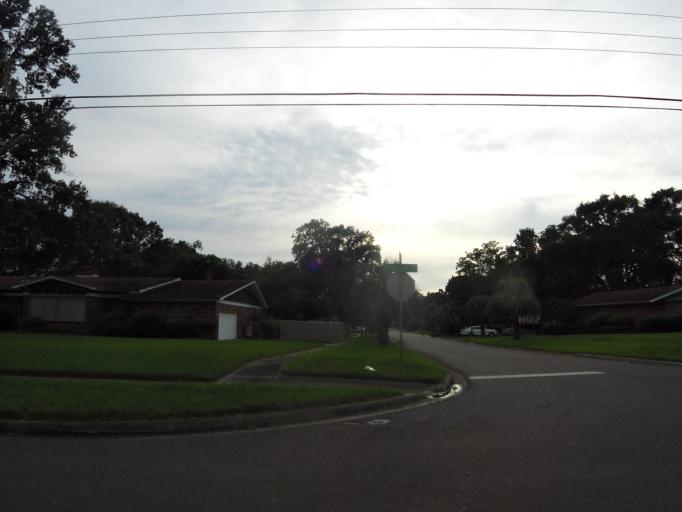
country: US
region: Florida
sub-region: Duval County
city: Jacksonville
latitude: 30.3869
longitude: -81.7250
